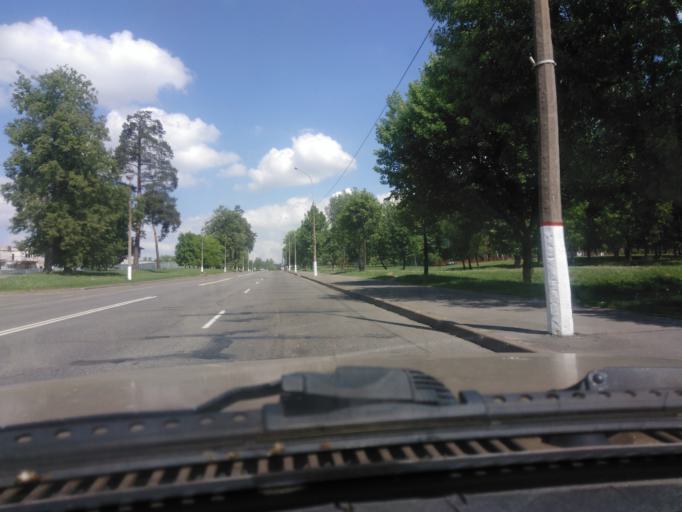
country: BY
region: Mogilev
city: Mahilyow
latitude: 53.9246
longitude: 30.3122
